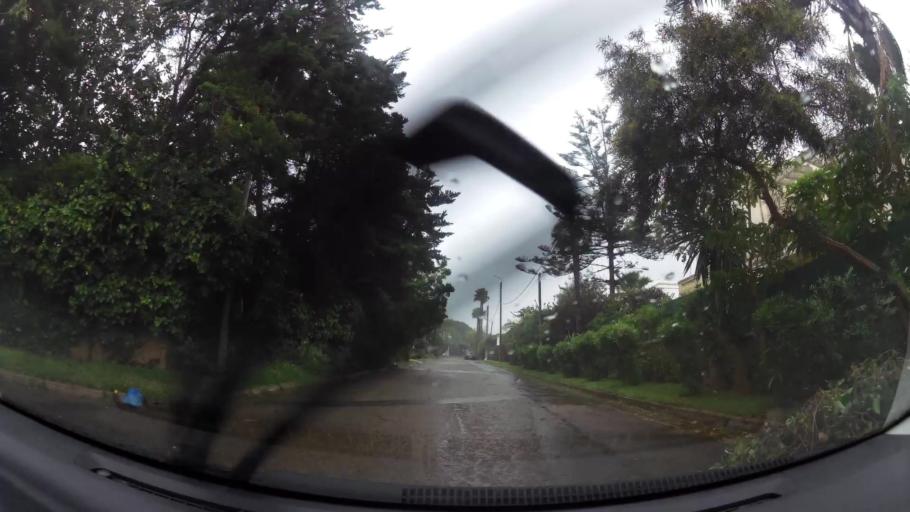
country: MA
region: Grand Casablanca
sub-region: Casablanca
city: Casablanca
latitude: 33.5871
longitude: -7.6771
